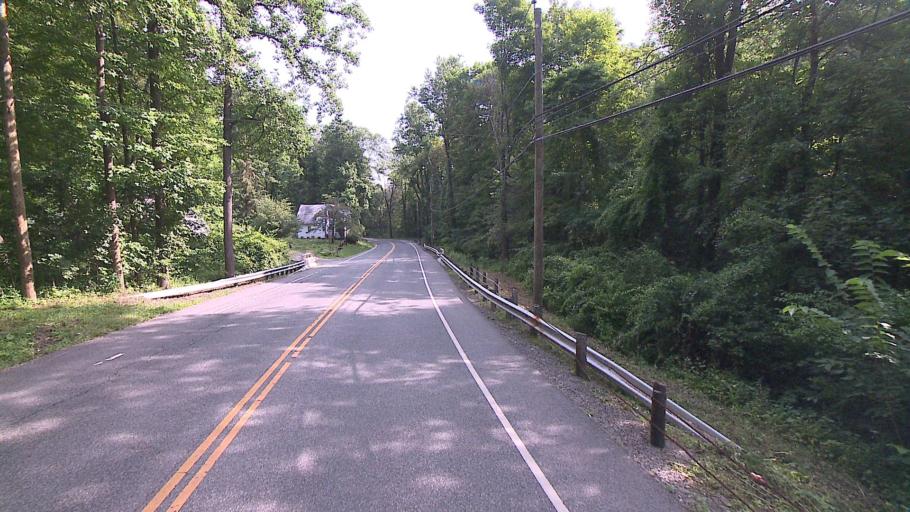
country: US
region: Connecticut
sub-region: Fairfield County
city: Sherman
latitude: 41.5699
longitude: -73.5068
